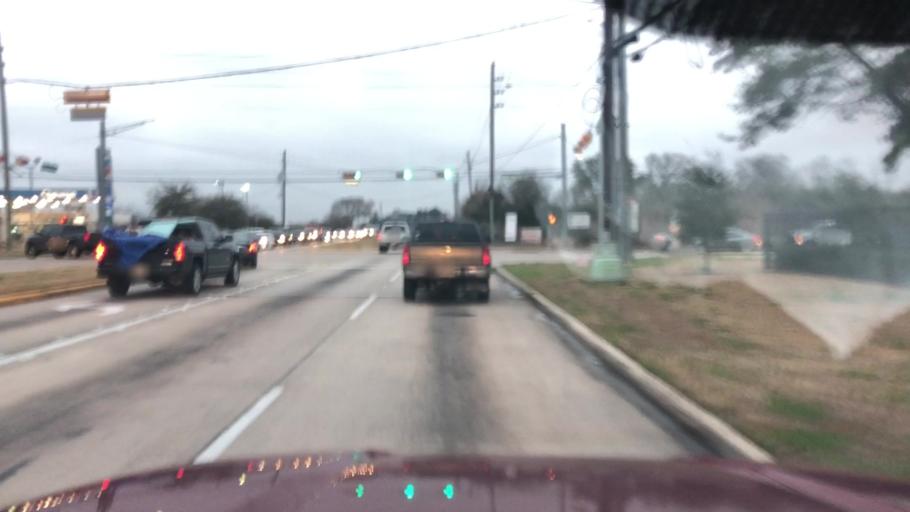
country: US
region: Texas
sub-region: Harris County
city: Tomball
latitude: 30.0455
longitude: -95.5383
